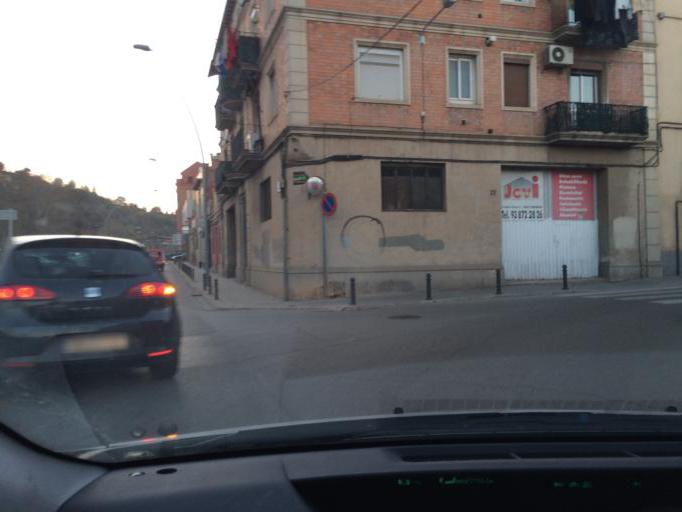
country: ES
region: Catalonia
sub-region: Provincia de Barcelona
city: Manresa
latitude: 41.7213
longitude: 1.8183
